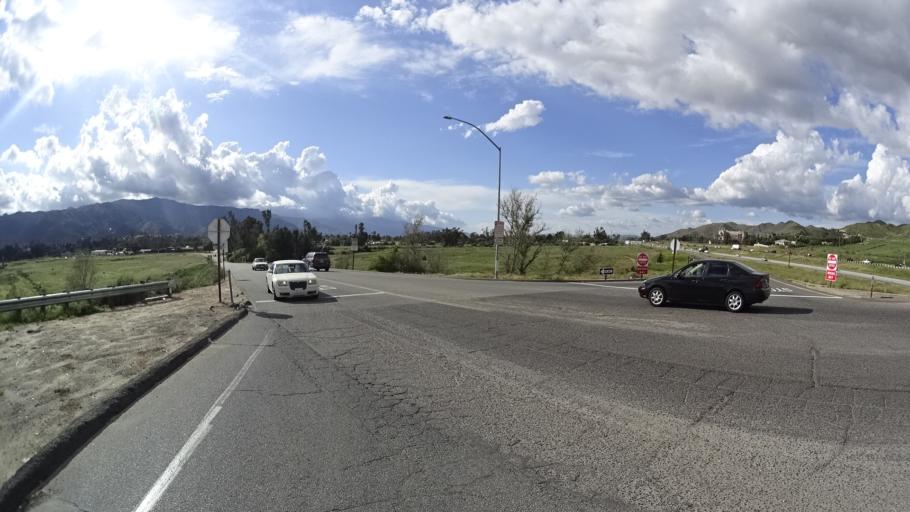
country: US
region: California
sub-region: Riverside County
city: Wildomar
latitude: 33.6124
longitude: -117.2614
